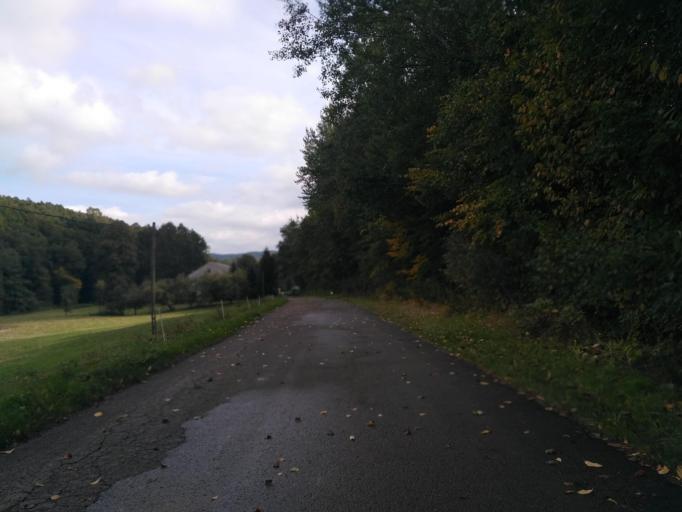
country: PL
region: Subcarpathian Voivodeship
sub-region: Powiat ropczycko-sedziszowski
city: Niedzwiada
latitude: 49.9334
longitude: 21.5347
